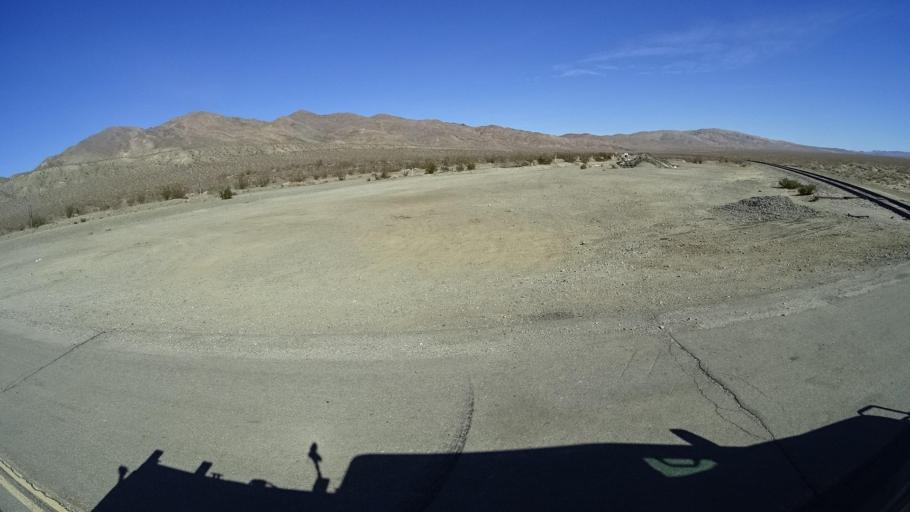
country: US
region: California
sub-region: Kern County
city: China Lake Acres
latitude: 35.3925
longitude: -117.7974
